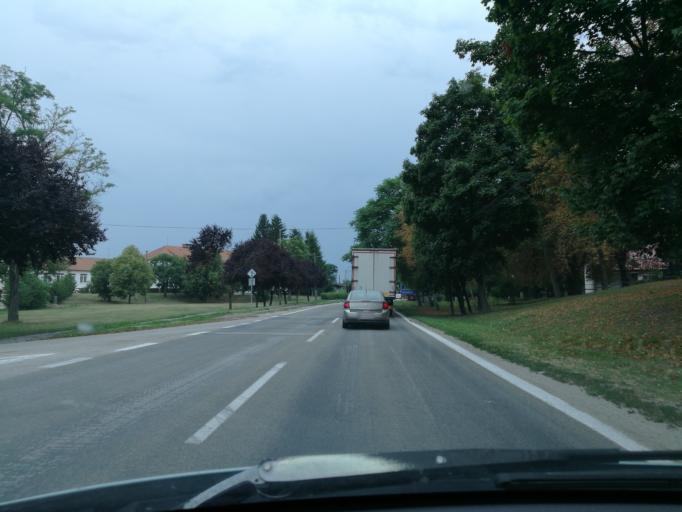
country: SK
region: Nitriansky
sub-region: Okres Komarno
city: Hurbanovo
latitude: 47.9288
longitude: 18.2070
